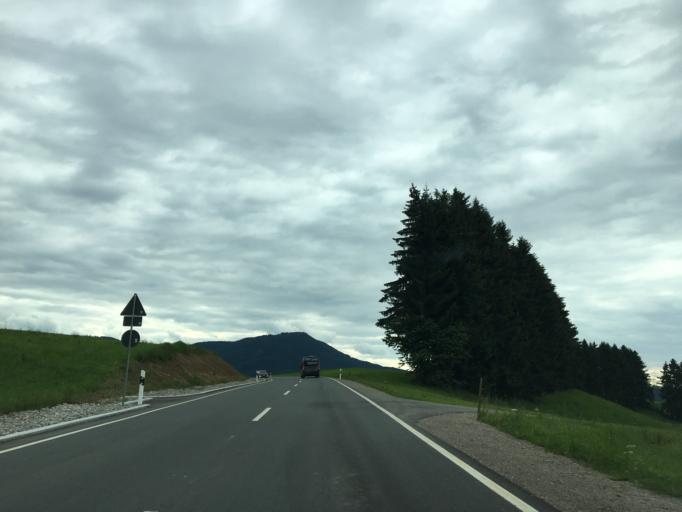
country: DE
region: Bavaria
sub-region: Upper Bavaria
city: Fischbachau
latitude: 47.7615
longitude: 11.9537
